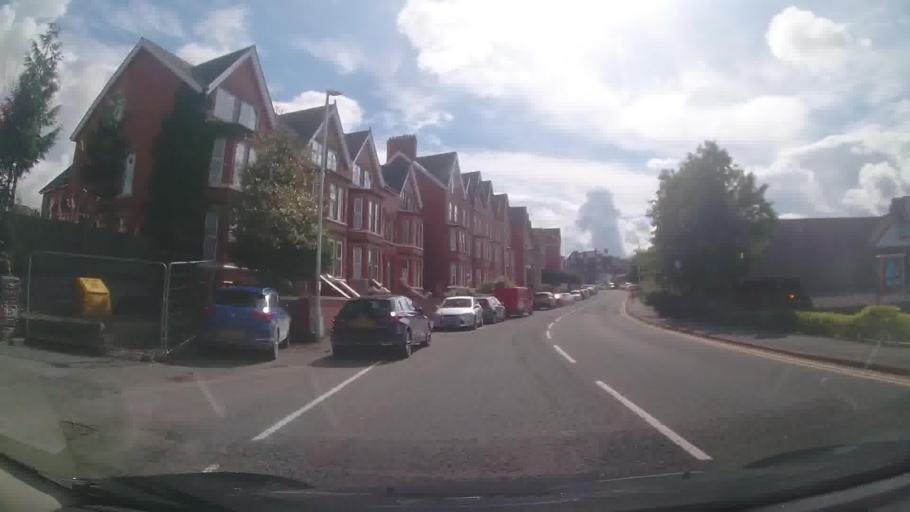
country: GB
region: Wales
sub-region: Sir Powys
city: Llandrindod Wells
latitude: 52.2431
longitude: -3.3773
